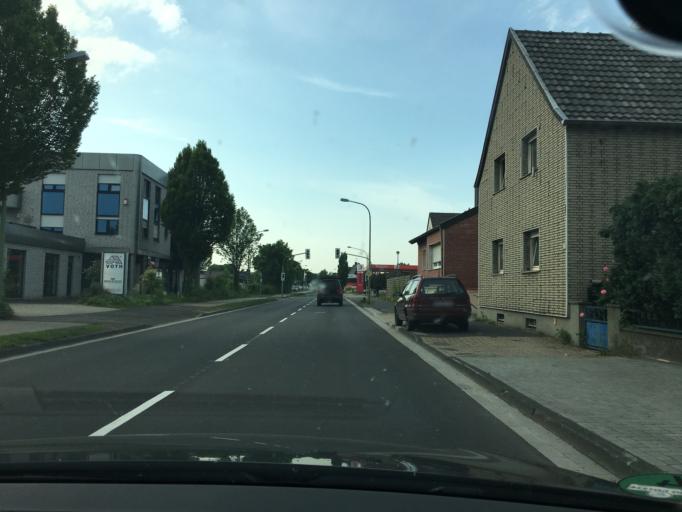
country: DE
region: North Rhine-Westphalia
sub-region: Regierungsbezirk Koln
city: Kreuzau
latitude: 50.7476
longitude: 6.4916
